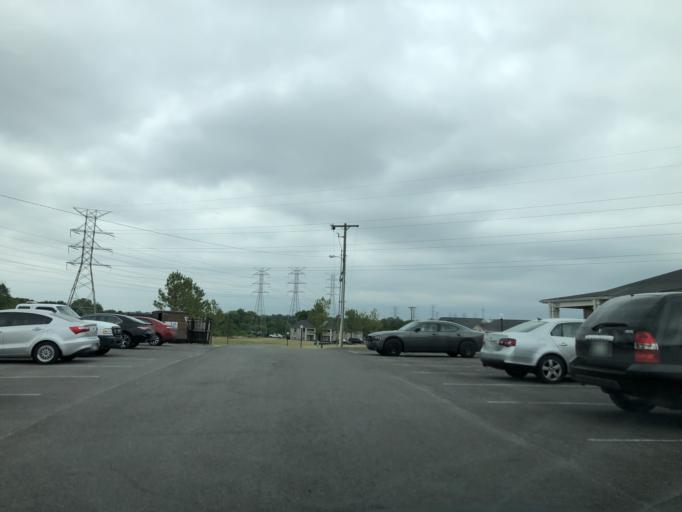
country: US
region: Tennessee
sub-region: Davidson County
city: Goodlettsville
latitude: 36.2897
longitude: -86.7207
